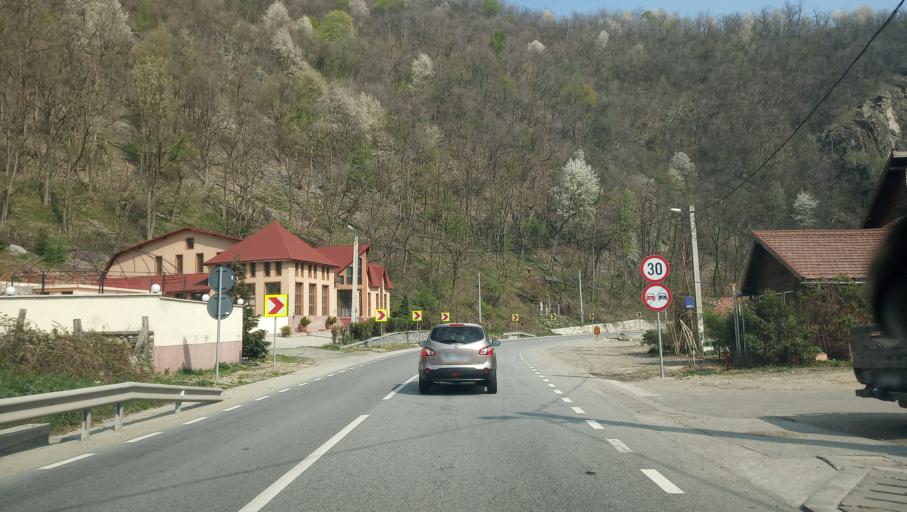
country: RO
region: Gorj
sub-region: Comuna Bumbesti-Jiu
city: Bumbesti-Jiu
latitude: 45.1921
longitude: 23.3881
